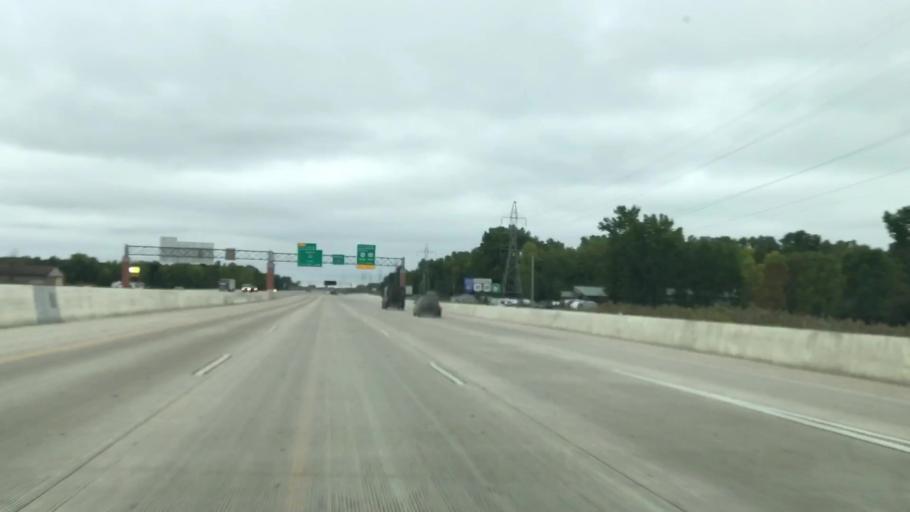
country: US
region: Wisconsin
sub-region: Brown County
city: Suamico
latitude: 44.5876
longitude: -88.0487
